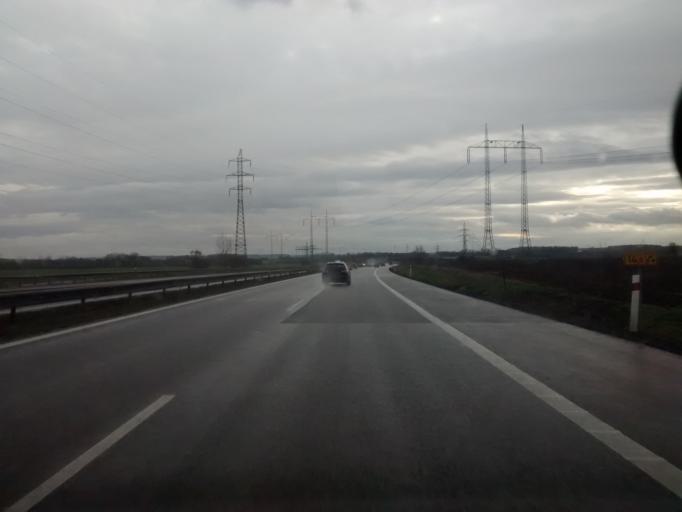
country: CZ
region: Central Bohemia
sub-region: Okres Melnik
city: Veltrusy
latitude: 50.2871
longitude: 14.3513
